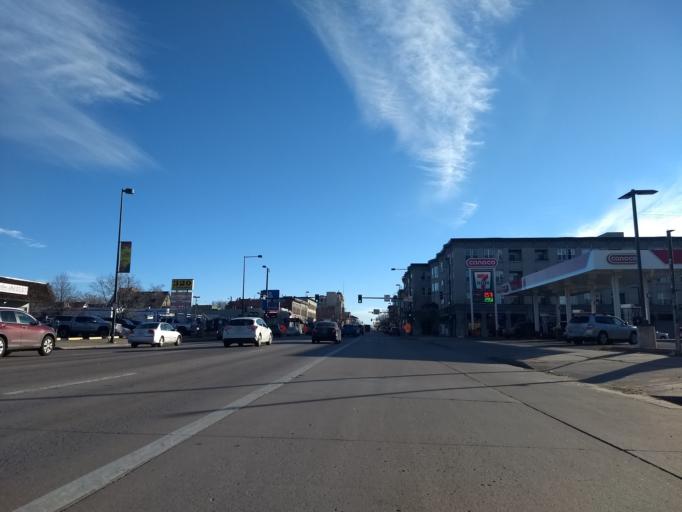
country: US
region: Colorado
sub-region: Denver County
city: Denver
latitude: 39.7216
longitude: -104.9876
